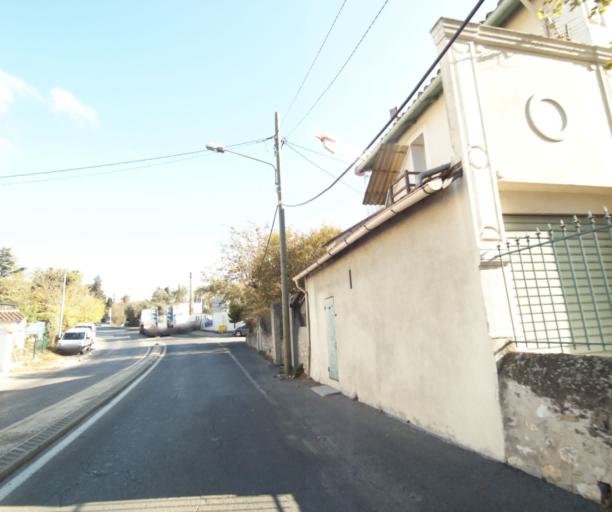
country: FR
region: Provence-Alpes-Cote d'Azur
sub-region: Departement des Bouches-du-Rhone
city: Allauch
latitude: 43.3376
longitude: 5.4792
